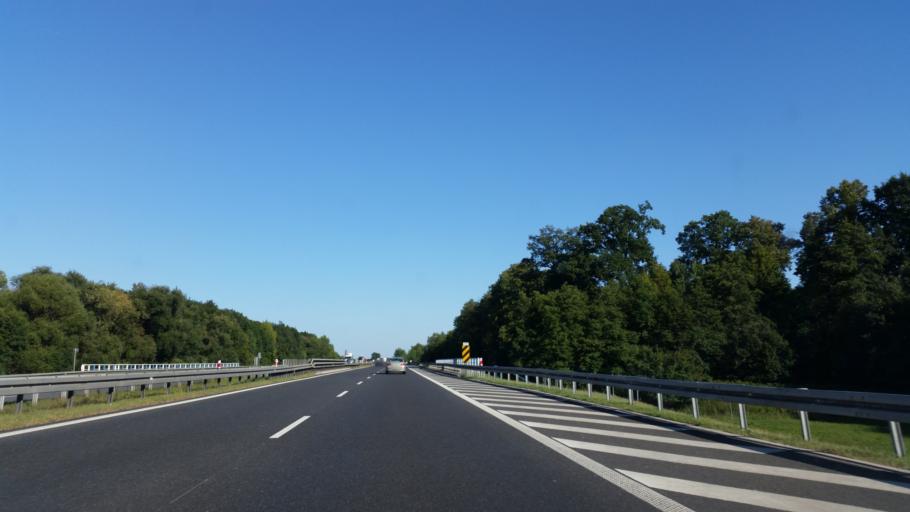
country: PL
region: Opole Voivodeship
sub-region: Powiat brzeski
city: Olszanka
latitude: 50.7300
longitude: 17.5075
